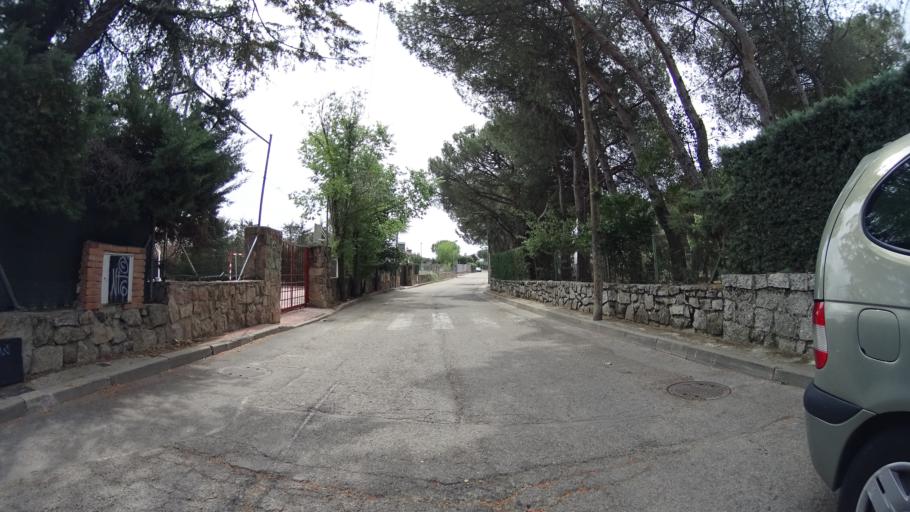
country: ES
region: Madrid
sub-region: Provincia de Madrid
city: Galapagar
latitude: 40.5708
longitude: -4.0013
